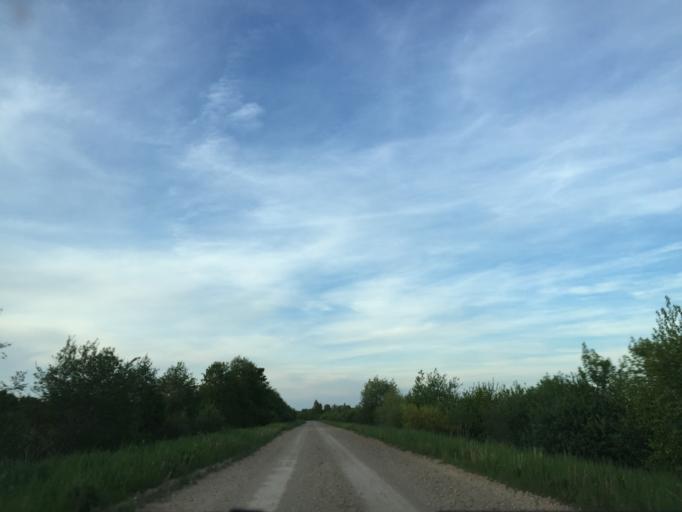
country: LV
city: Tireli
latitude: 56.7412
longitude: 23.5189
